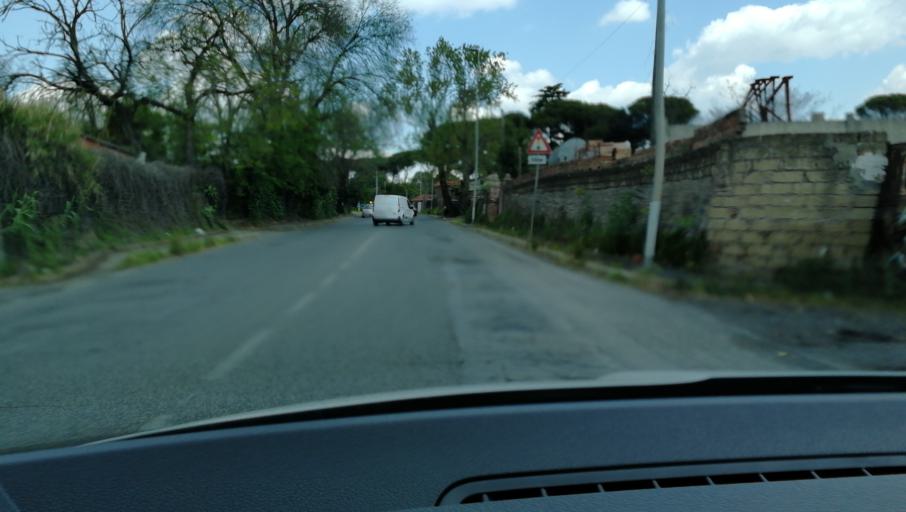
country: IT
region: Latium
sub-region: Citta metropolitana di Roma Capitale
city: Rome
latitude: 41.8595
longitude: 12.5332
